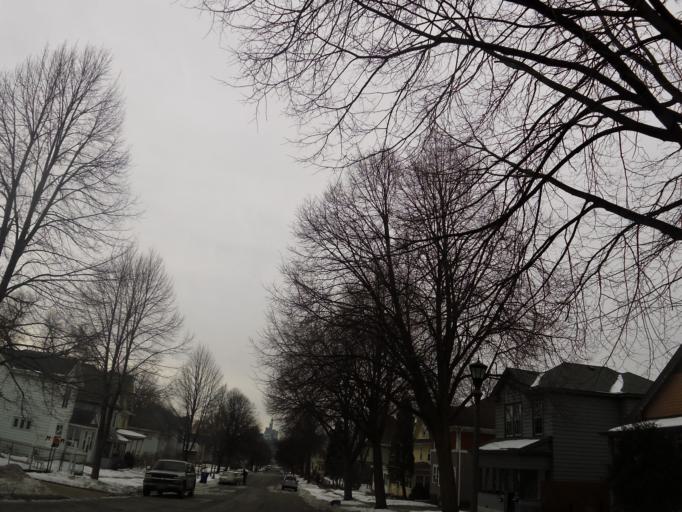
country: US
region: Minnesota
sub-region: Ramsey County
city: Saint Paul
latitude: 44.9576
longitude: -93.0687
